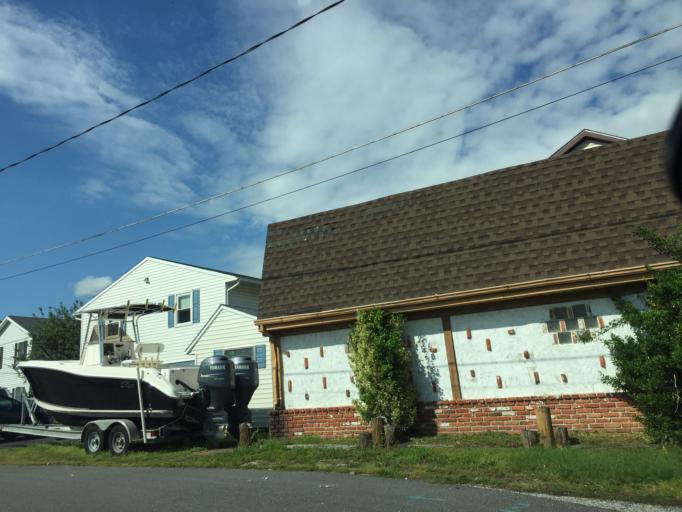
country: US
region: Maryland
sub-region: Baltimore County
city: Middle River
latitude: 39.3167
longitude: -76.4269
